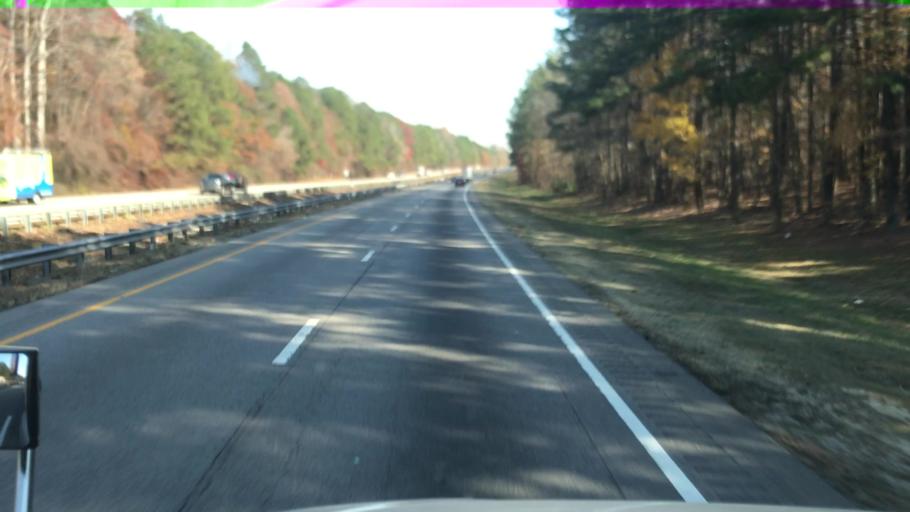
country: US
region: North Carolina
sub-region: Wake County
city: Wendell
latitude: 35.8209
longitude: -78.3891
